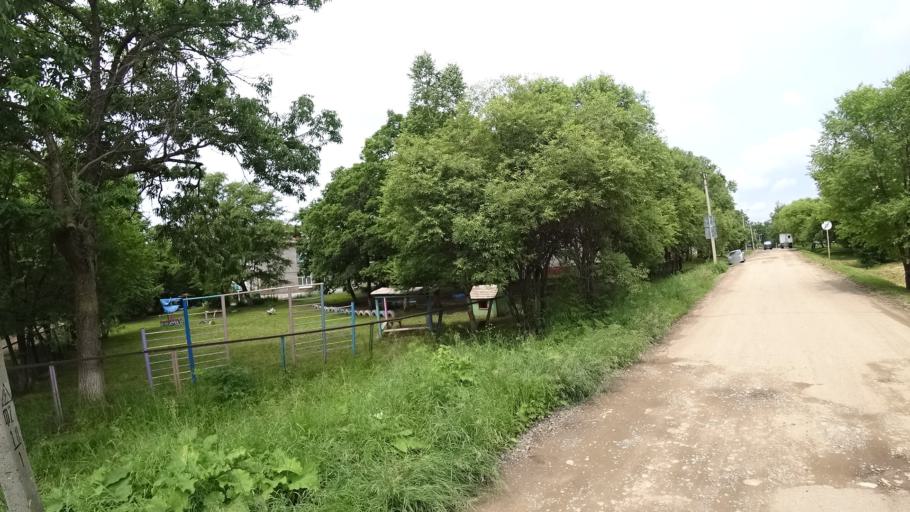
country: RU
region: Primorskiy
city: Novosysoyevka
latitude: 44.2270
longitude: 133.3616
